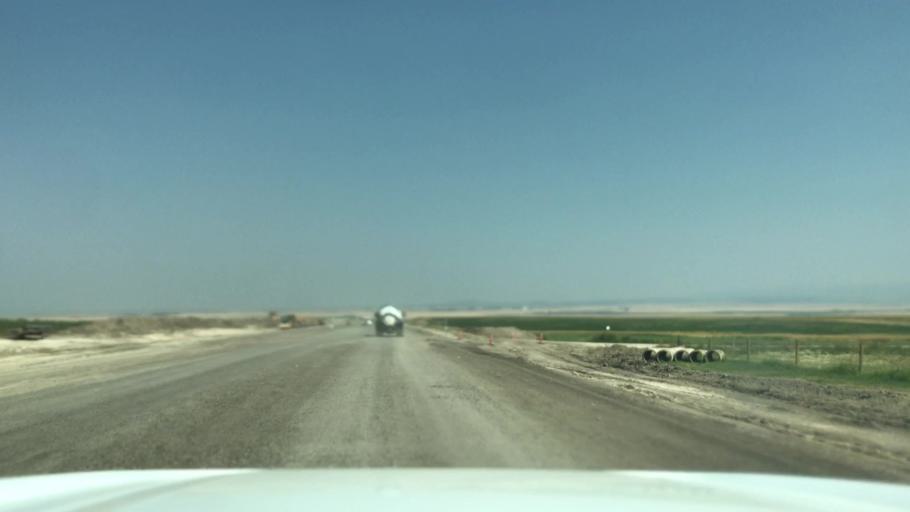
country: US
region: Montana
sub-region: Fergus County
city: Lewistown
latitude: 46.9991
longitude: -109.8199
